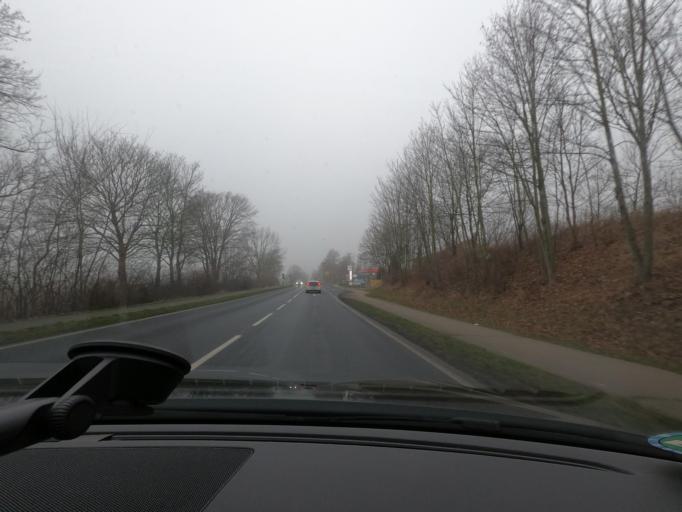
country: DE
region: North Rhine-Westphalia
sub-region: Regierungsbezirk Koln
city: Merzenich
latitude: 50.8200
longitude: 6.5343
